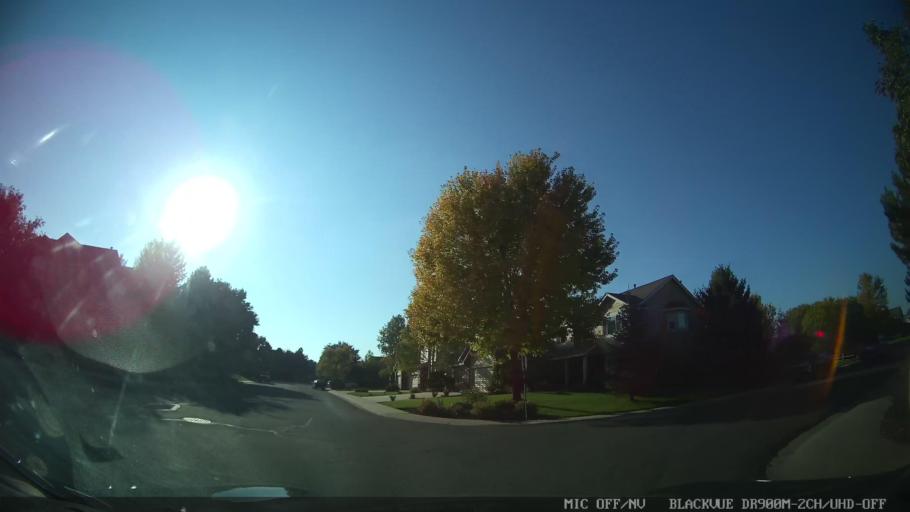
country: US
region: Colorado
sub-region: Larimer County
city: Fort Collins
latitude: 40.5090
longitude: -105.0404
